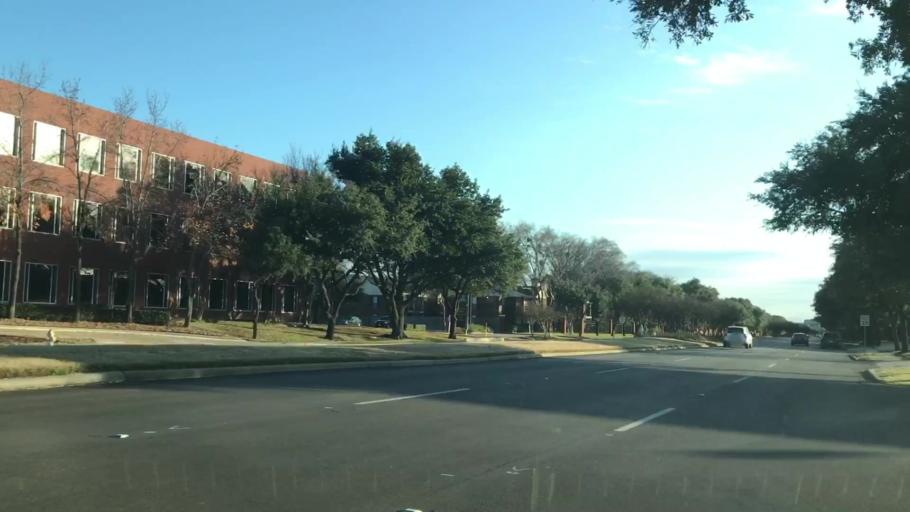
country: US
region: Texas
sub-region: Dallas County
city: Farmers Branch
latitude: 32.9403
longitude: -96.9522
